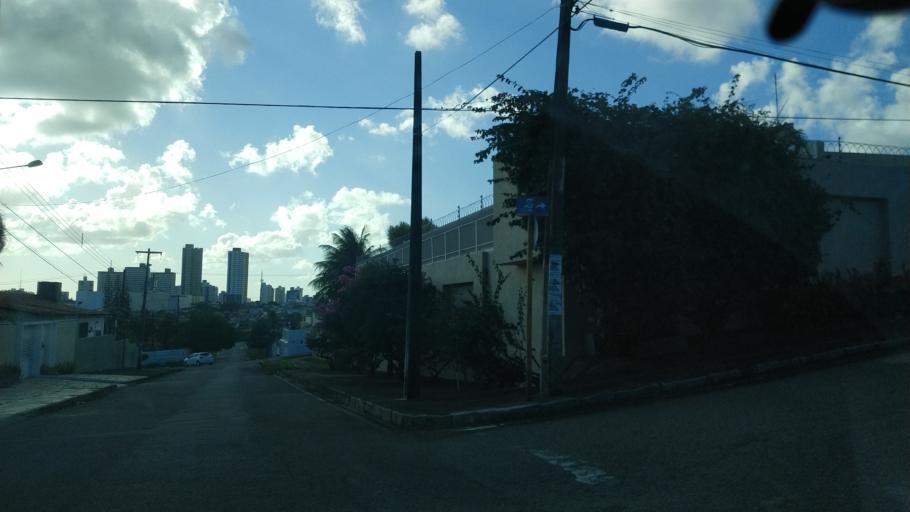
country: BR
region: Rio Grande do Norte
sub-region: Natal
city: Natal
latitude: -5.8473
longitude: -35.2052
